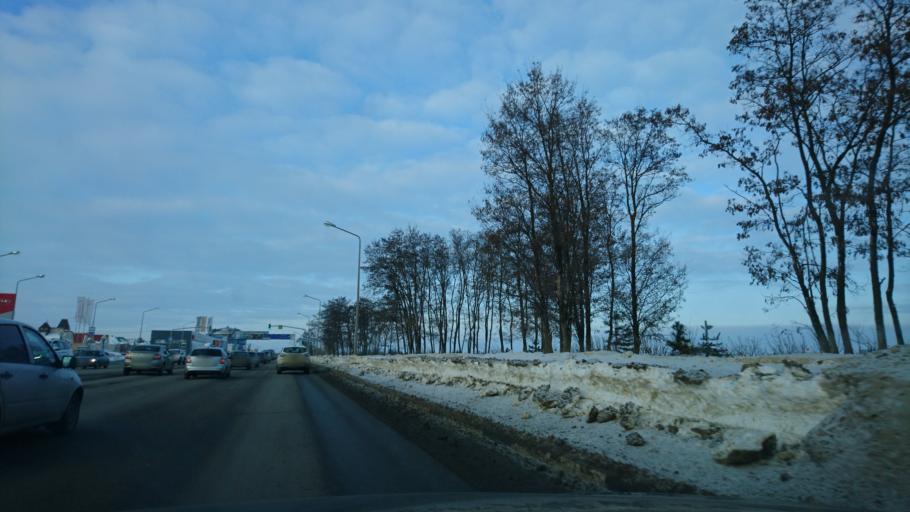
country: RU
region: Belgorod
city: Severnyy
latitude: 50.6509
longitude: 36.5667
